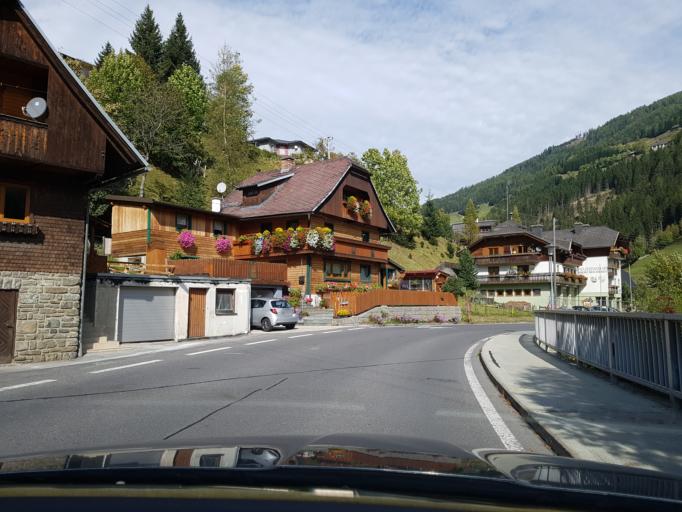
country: AT
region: Carinthia
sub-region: Politischer Bezirk Spittal an der Drau
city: Kleinkirchheim
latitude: 46.8564
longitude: 13.8915
